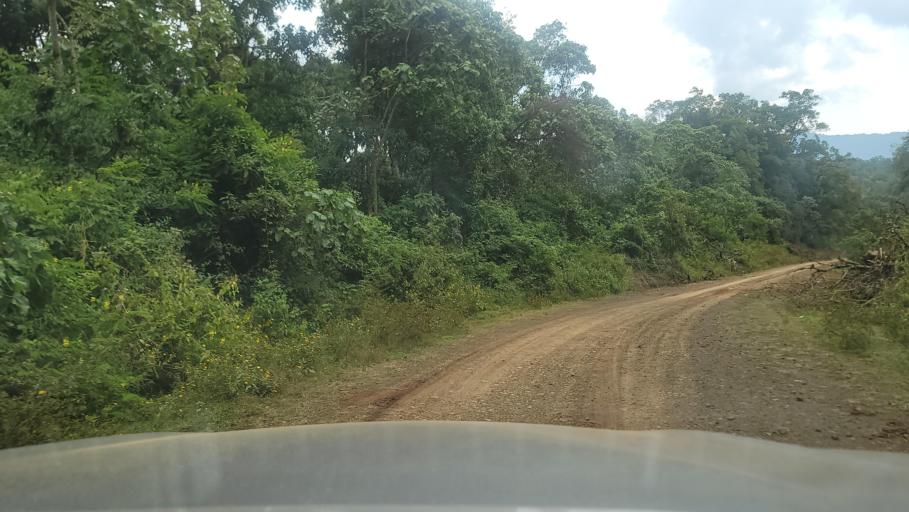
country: ET
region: Southern Nations, Nationalities, and People's Region
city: Bonga
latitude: 7.6635
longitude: 36.2455
